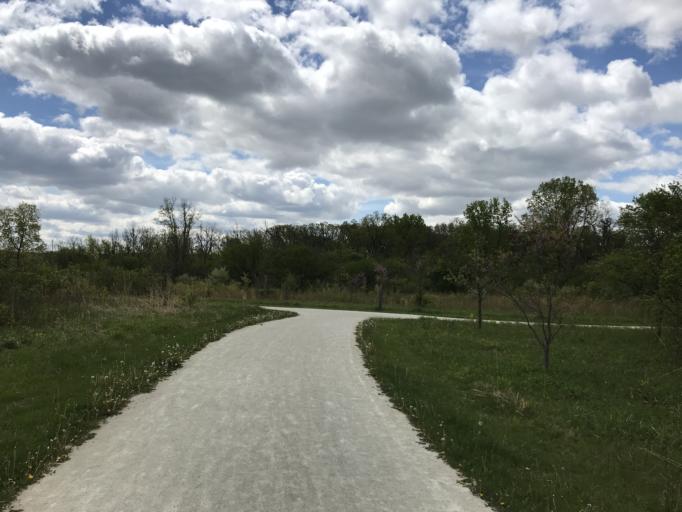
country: US
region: Illinois
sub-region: DuPage County
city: Woodridge
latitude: 41.7402
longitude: -88.0845
